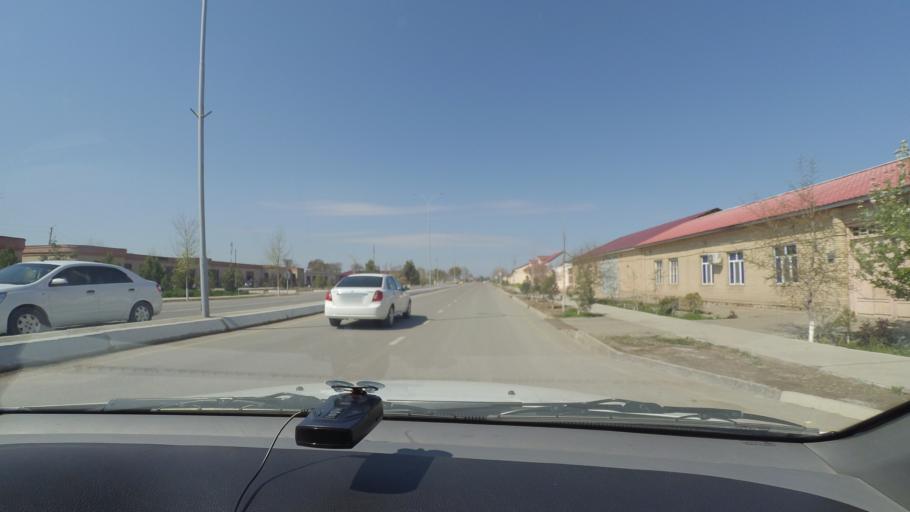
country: UZ
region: Bukhara
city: Kogon
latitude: 39.8001
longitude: 64.5303
